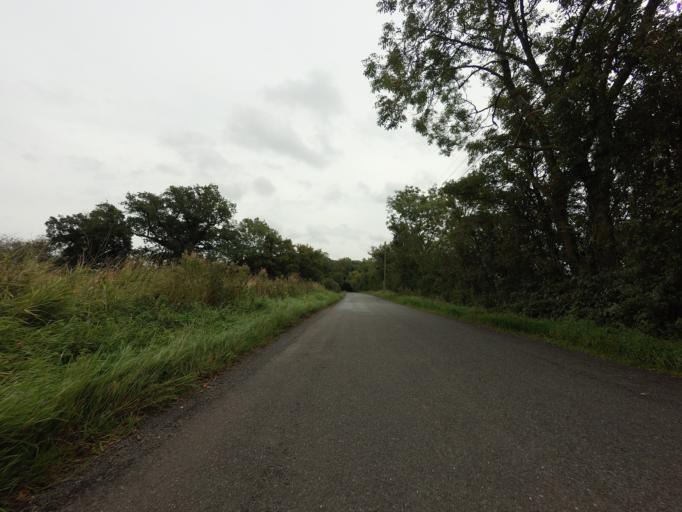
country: GB
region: England
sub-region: Hertfordshire
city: Buntingford
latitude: 51.9716
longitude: 0.0867
